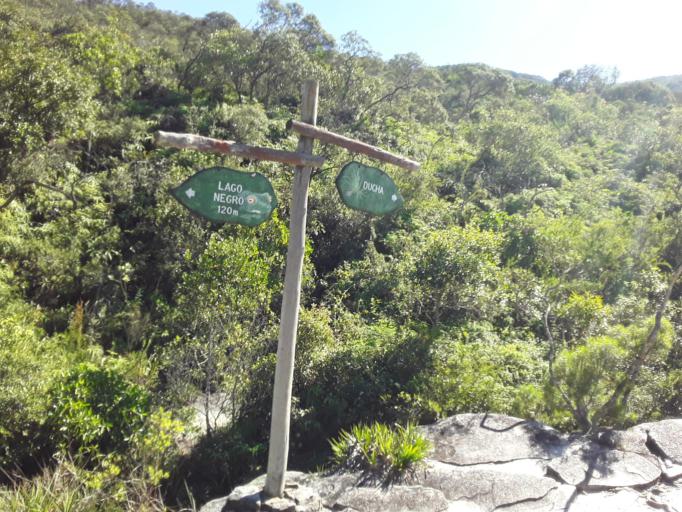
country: BR
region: Minas Gerais
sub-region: Lima Duarte
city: Lima Duarte
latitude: -21.7057
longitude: -43.8938
